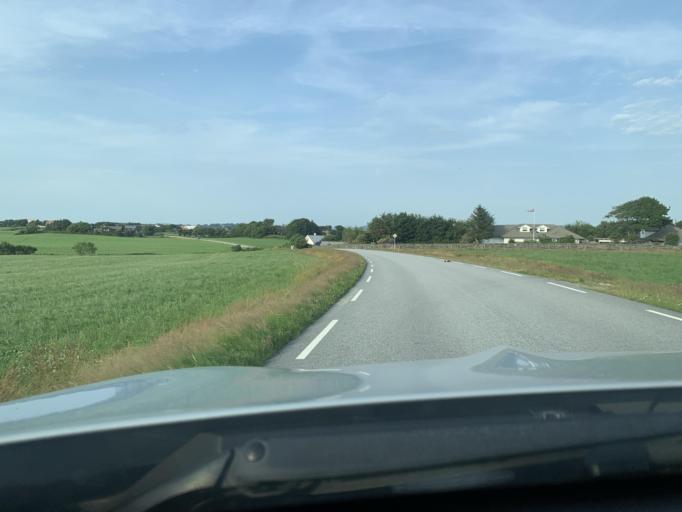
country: NO
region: Rogaland
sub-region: Time
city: Bryne
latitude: 58.7242
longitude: 5.5807
